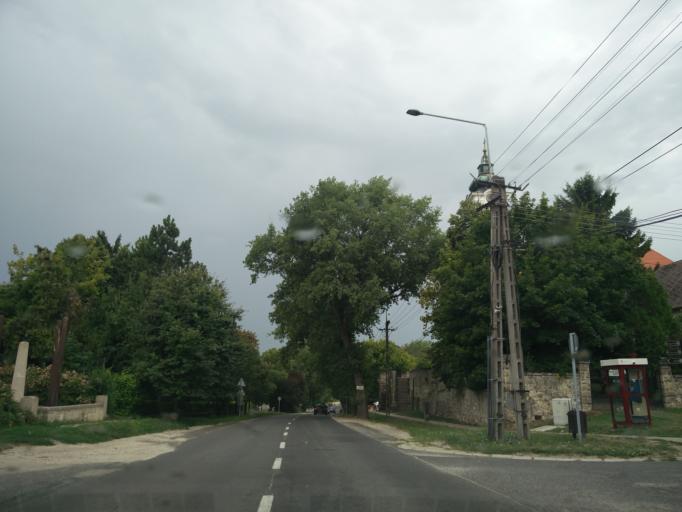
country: HU
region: Fejer
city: Etyek
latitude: 47.4455
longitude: 18.7522
